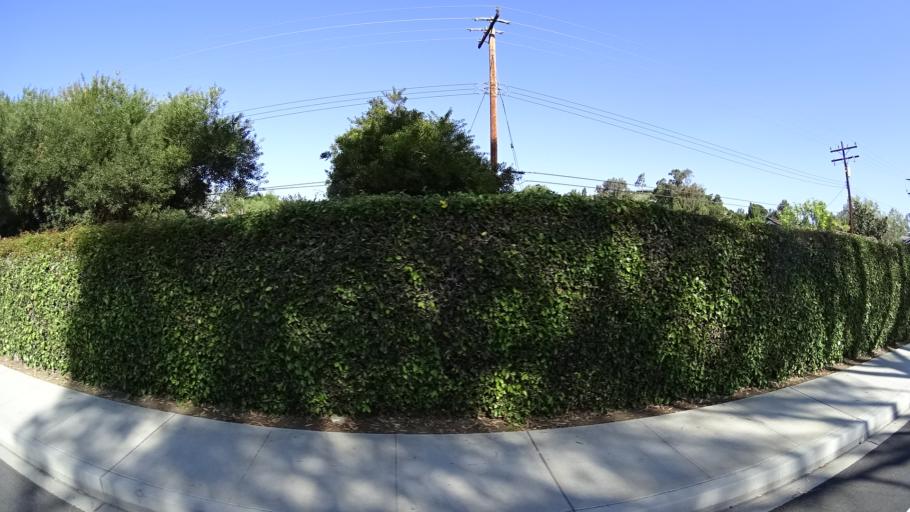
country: US
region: California
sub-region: Ventura County
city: Casa Conejo
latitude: 34.1952
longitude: -118.8924
